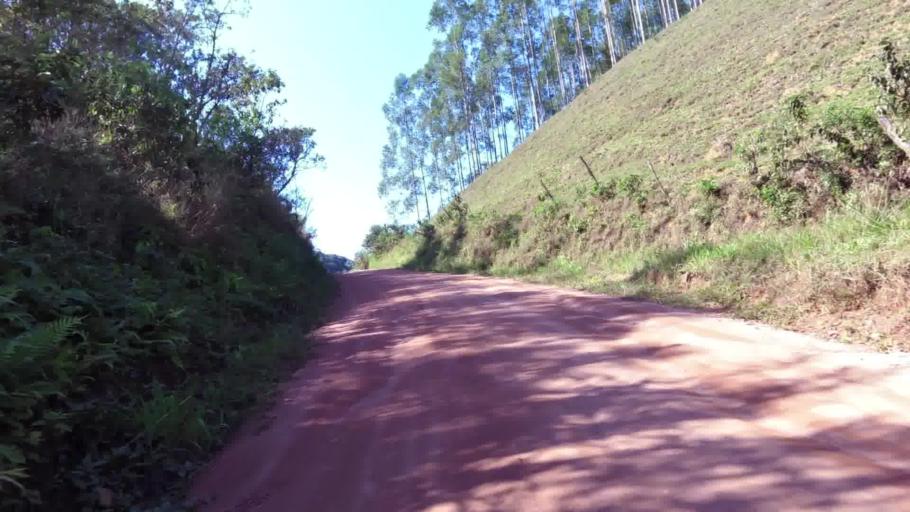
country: BR
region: Espirito Santo
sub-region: Alfredo Chaves
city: Alfredo Chaves
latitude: -20.5649
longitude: -40.7766
